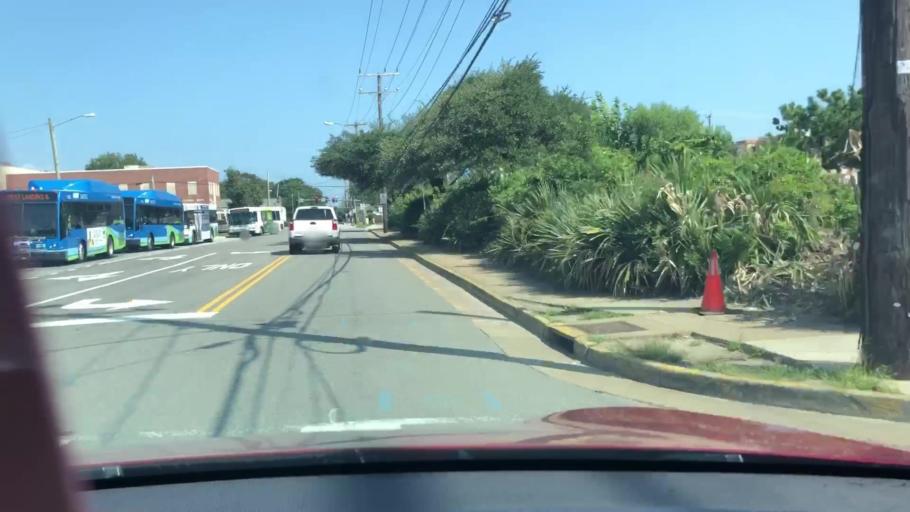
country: US
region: Virginia
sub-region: City of Virginia Beach
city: Virginia Beach
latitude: 36.8468
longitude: -75.9779
